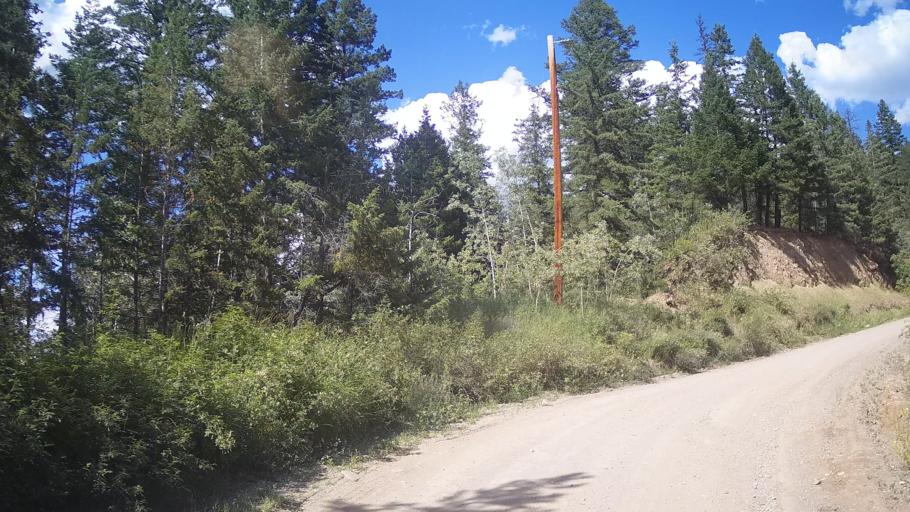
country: CA
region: British Columbia
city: Lillooet
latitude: 51.2619
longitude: -121.9849
